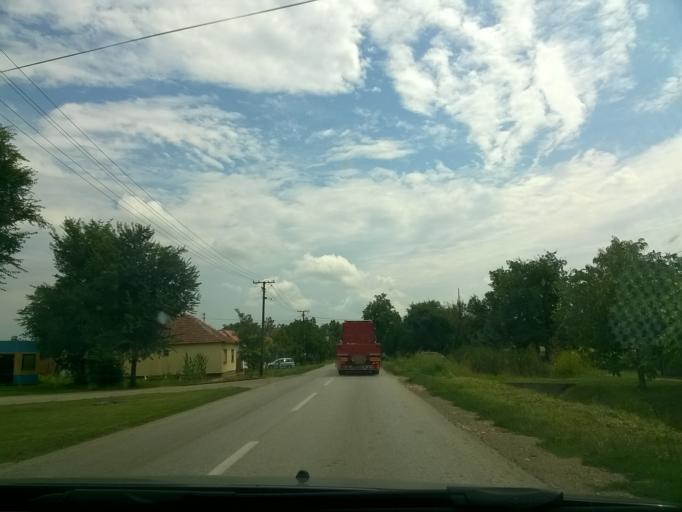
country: RS
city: Lazarevo
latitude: 45.3871
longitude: 20.5267
